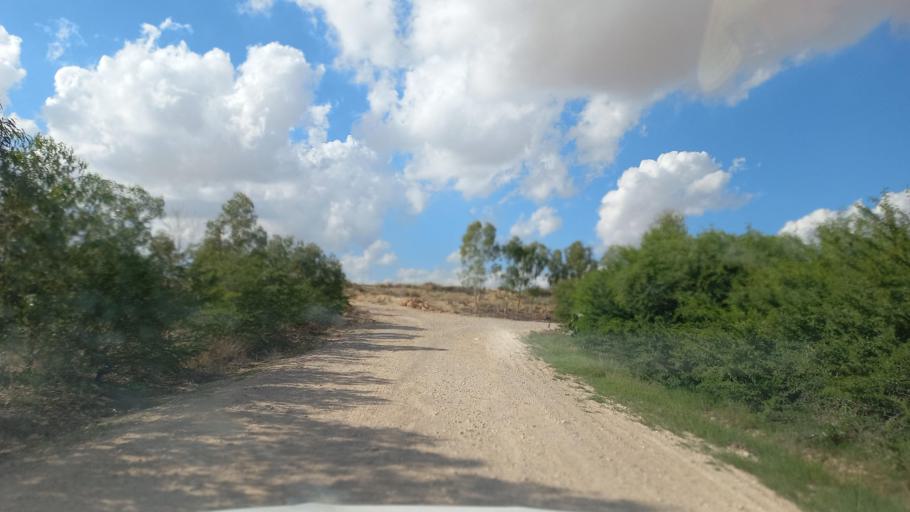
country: TN
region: Al Qasrayn
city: Sbiba
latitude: 35.3408
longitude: 9.0760
